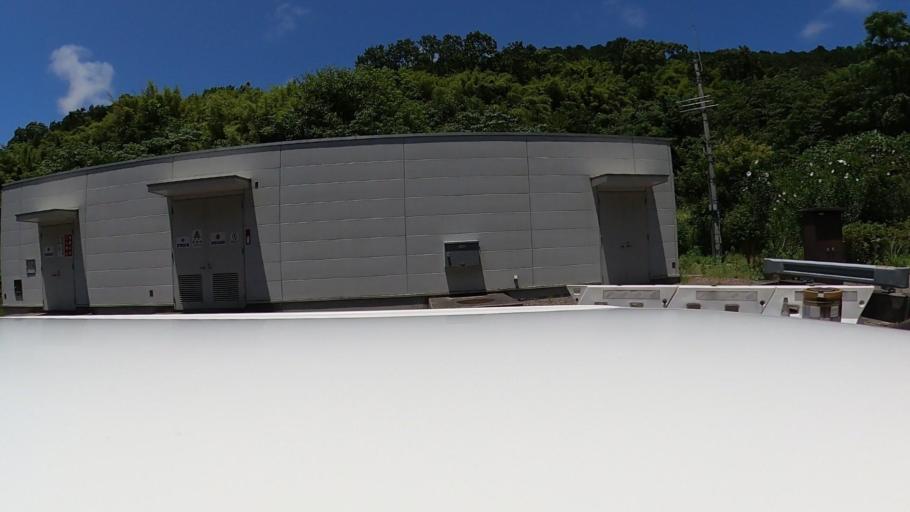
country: JP
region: Miyazaki
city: Nobeoka
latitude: 32.3525
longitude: 131.6085
